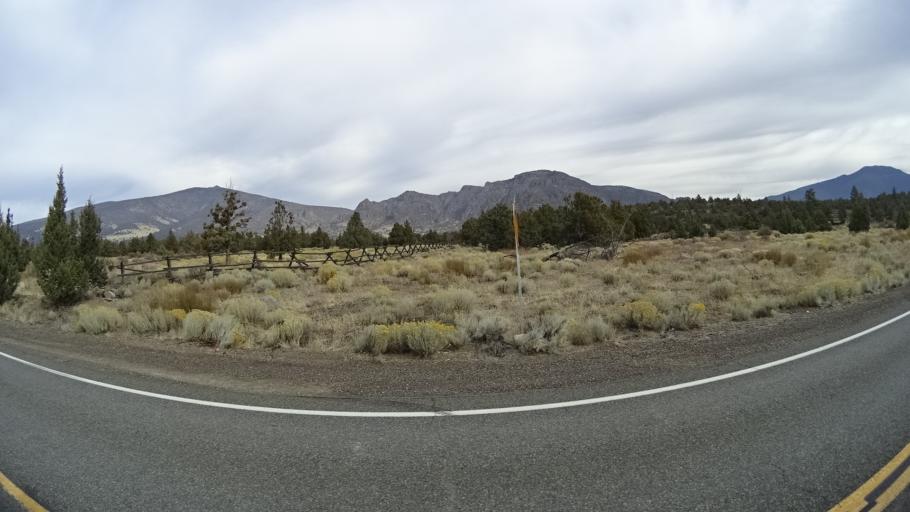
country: US
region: California
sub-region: Siskiyou County
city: Weed
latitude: 41.5669
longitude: -122.2661
